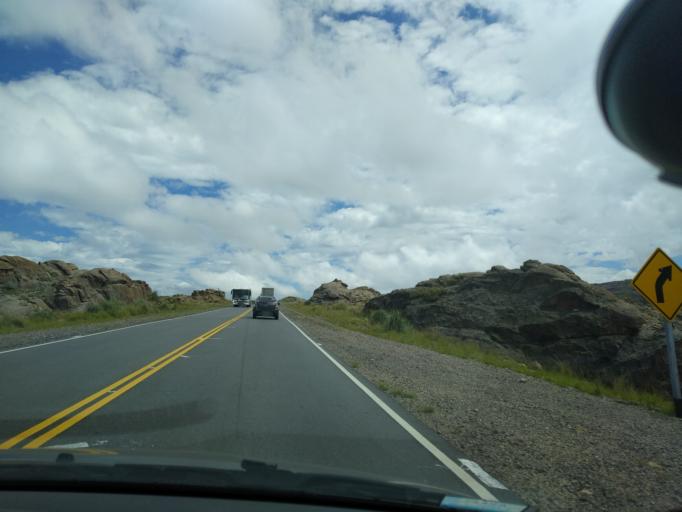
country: AR
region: Cordoba
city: Mina Clavero
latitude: -31.6880
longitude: -64.8982
